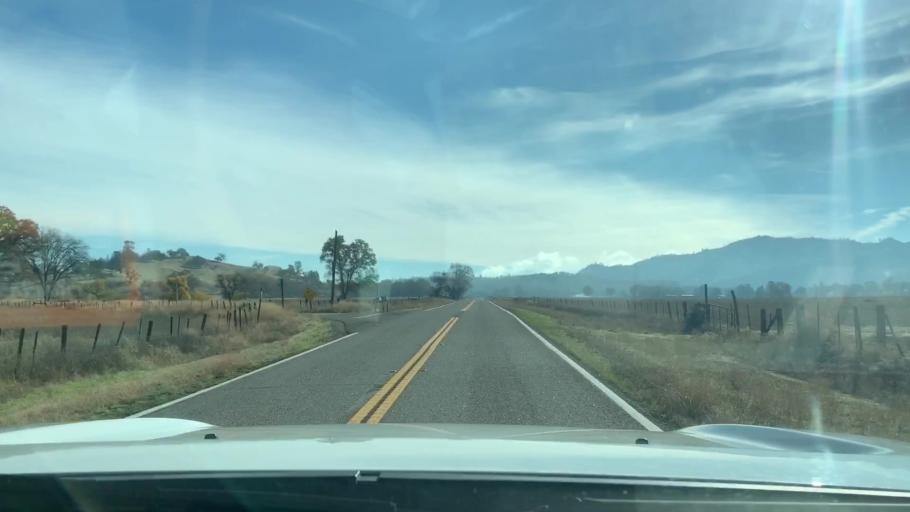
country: US
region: California
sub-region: Fresno County
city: Coalinga
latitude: 36.1834
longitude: -120.7001
